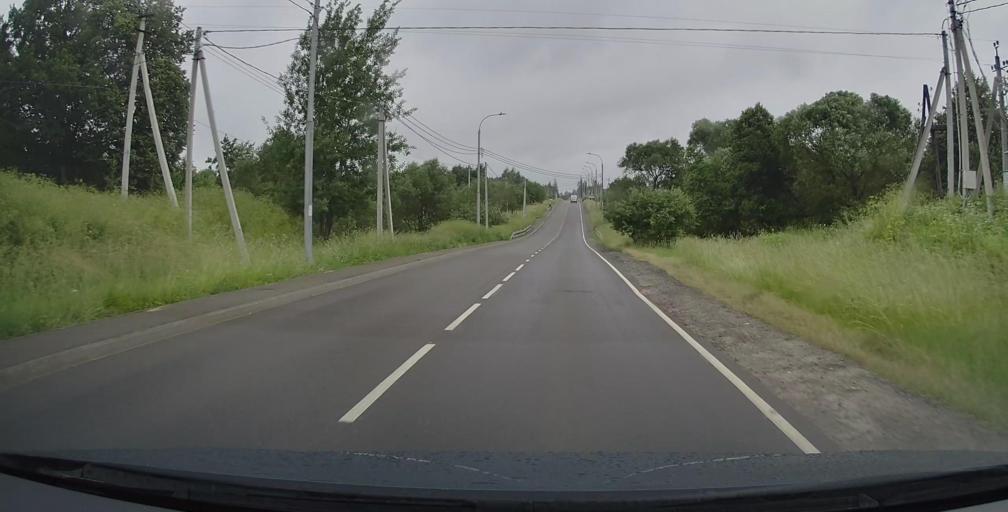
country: RU
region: Moskovskaya
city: Selyatino
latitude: 55.4112
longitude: 37.0127
